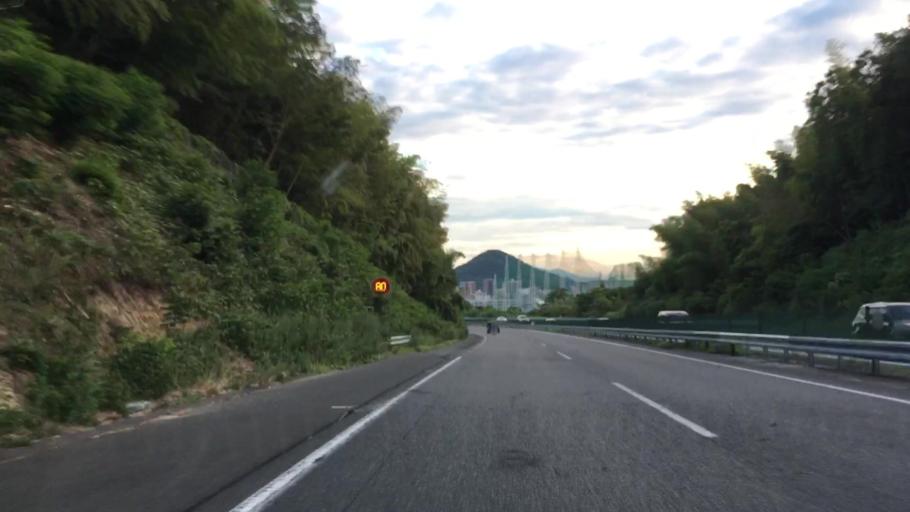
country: JP
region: Yamaguchi
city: Shimonoseki
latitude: 34.0214
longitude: 130.9594
